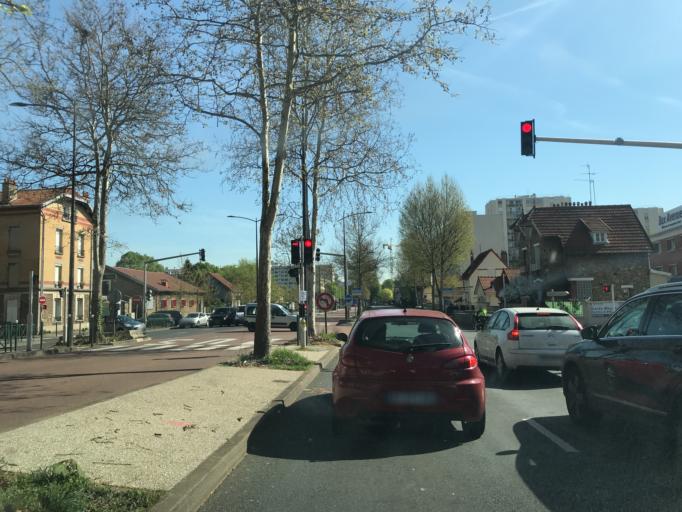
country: FR
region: Ile-de-France
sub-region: Departement du Val-de-Marne
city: Thiais
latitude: 48.7593
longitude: 2.3961
